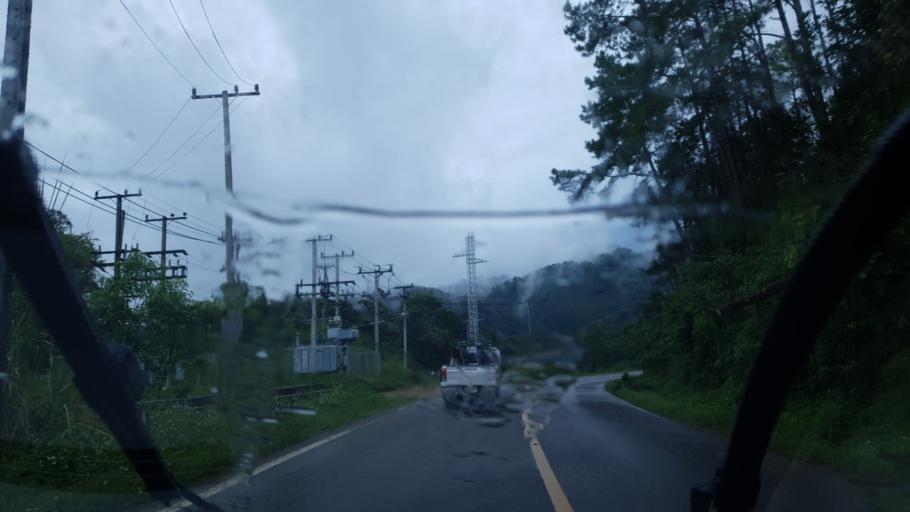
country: TH
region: Mae Hong Son
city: Ban Huai I Huak
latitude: 18.1635
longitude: 98.0391
